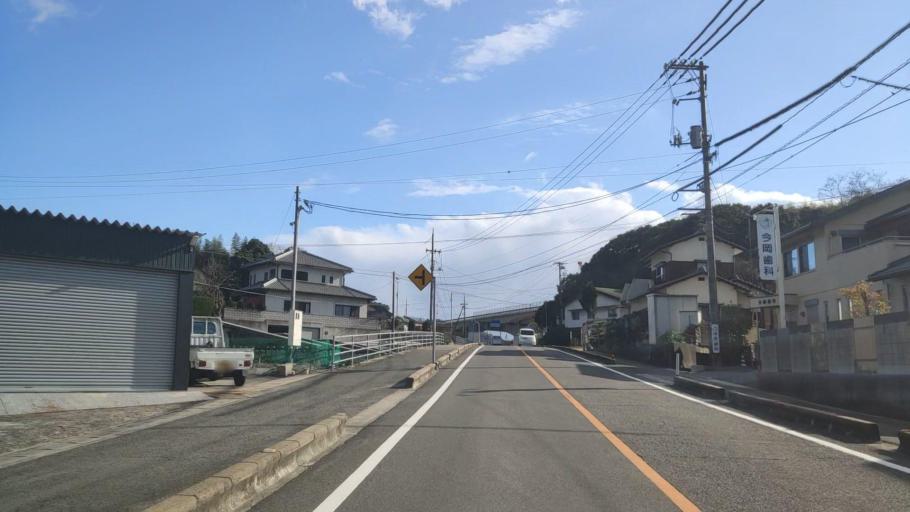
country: JP
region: Hiroshima
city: Innoshima
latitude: 34.2151
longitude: 133.0676
